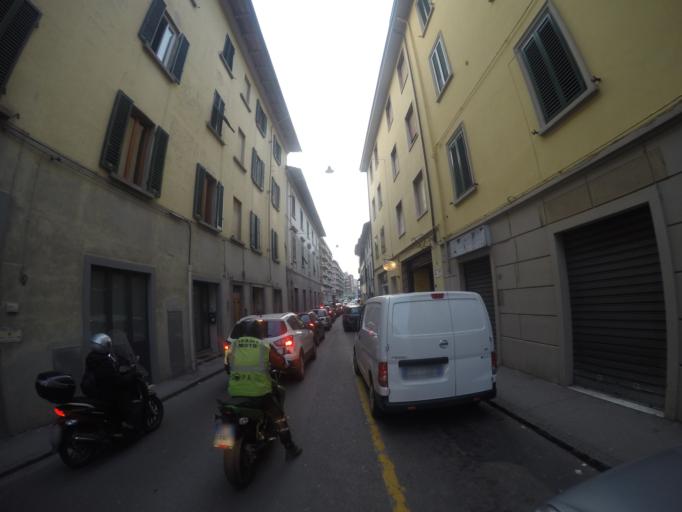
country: IT
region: Tuscany
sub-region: Provincia di Prato
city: Prato
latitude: 43.8856
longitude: 11.0952
